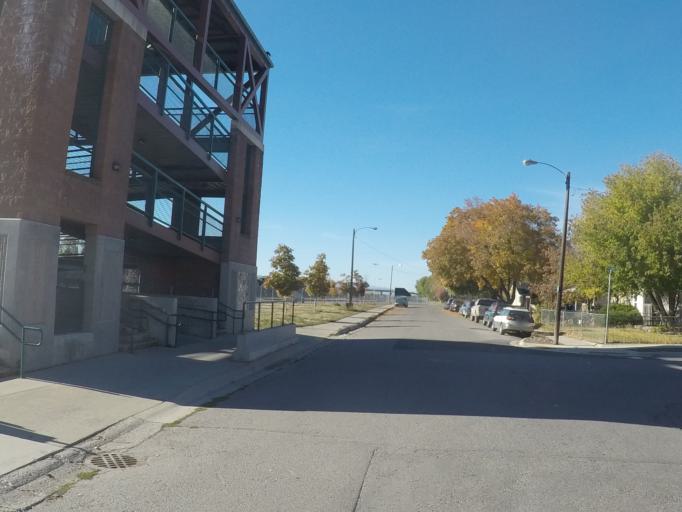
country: US
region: Montana
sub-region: Missoula County
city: Missoula
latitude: 46.8785
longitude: -113.9961
